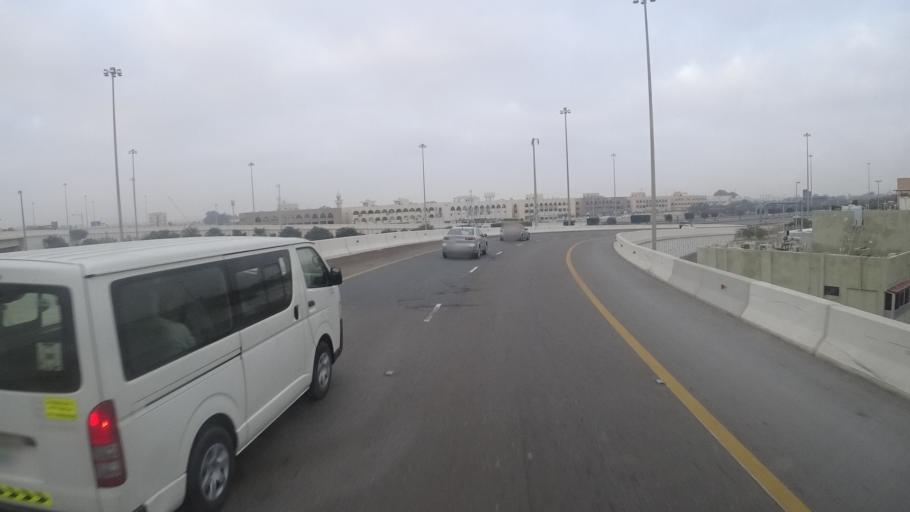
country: AE
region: Abu Dhabi
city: Abu Dhabi
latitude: 24.2821
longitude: 54.6482
